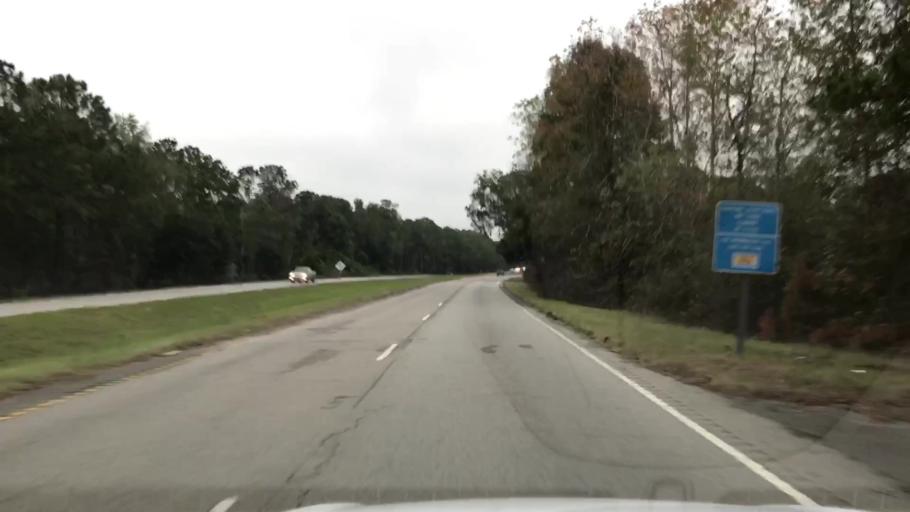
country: US
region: South Carolina
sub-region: Charleston County
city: Awendaw
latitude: 33.0305
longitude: -79.6249
